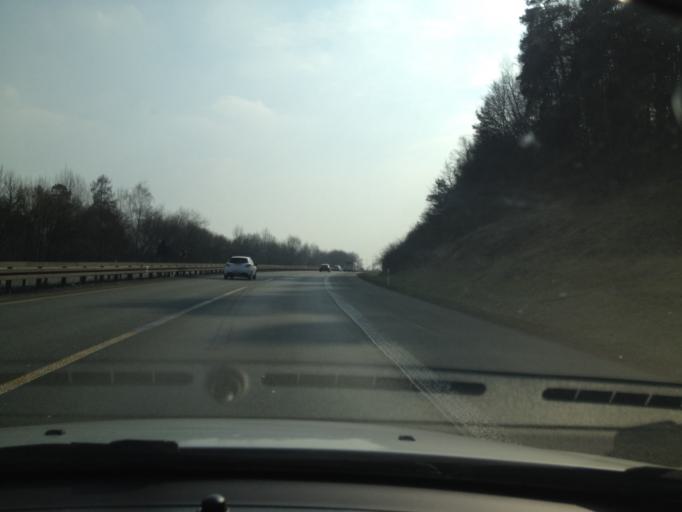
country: DE
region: Hesse
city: Herborn
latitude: 50.6931
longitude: 8.2955
